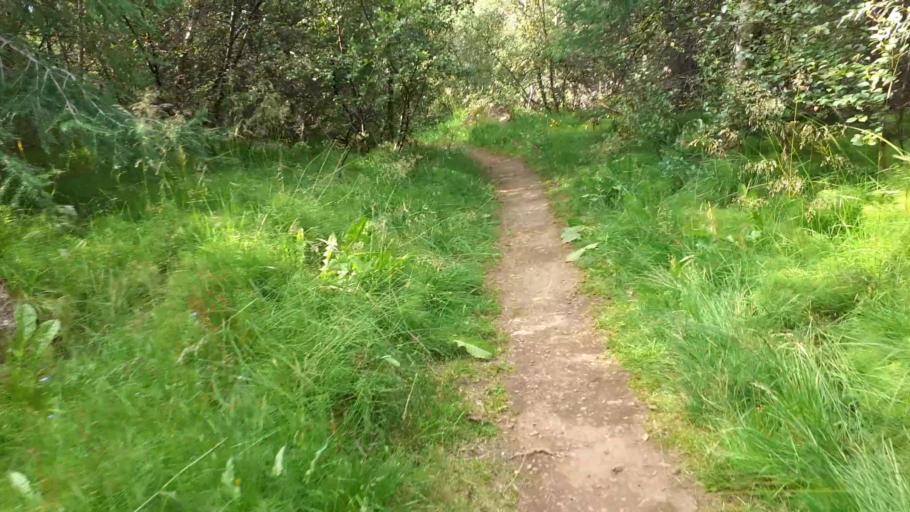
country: IS
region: Northeast
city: Akureyri
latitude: 65.6397
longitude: -18.0944
